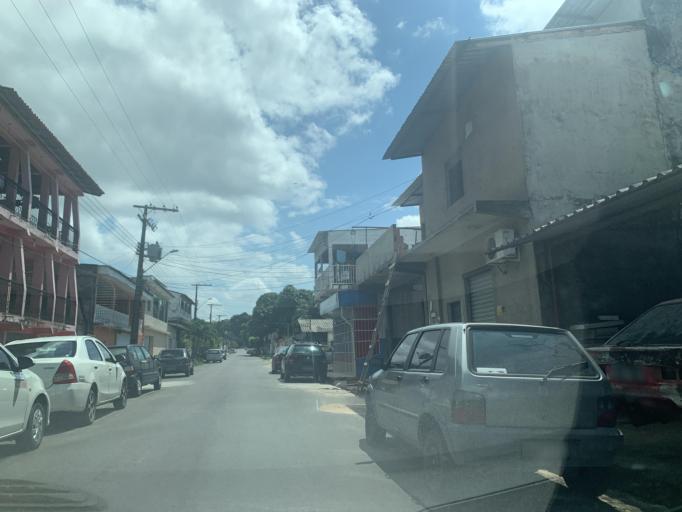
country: BR
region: Amazonas
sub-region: Manaus
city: Manaus
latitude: -3.1042
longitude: -59.9629
